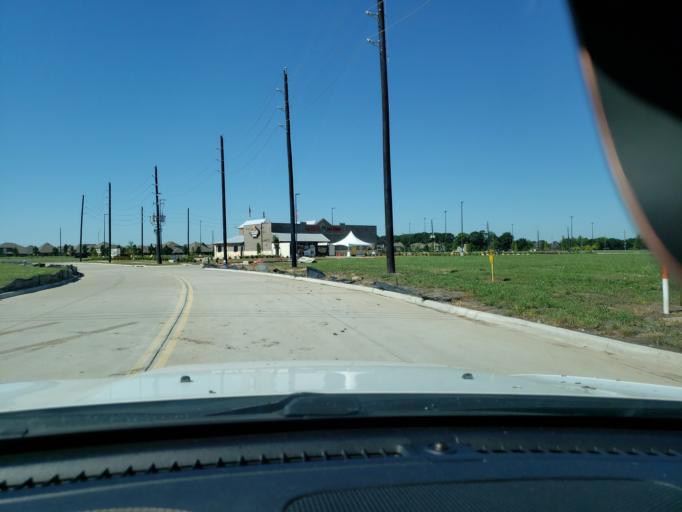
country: US
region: Texas
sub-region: Fort Bend County
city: Pecan Grove
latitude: 29.6618
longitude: -95.7217
